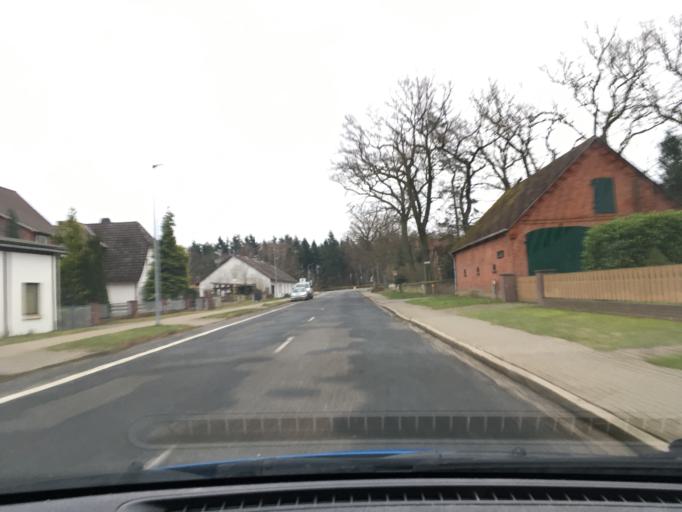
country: DE
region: Lower Saxony
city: Tosterglope
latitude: 53.2648
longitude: 10.8036
